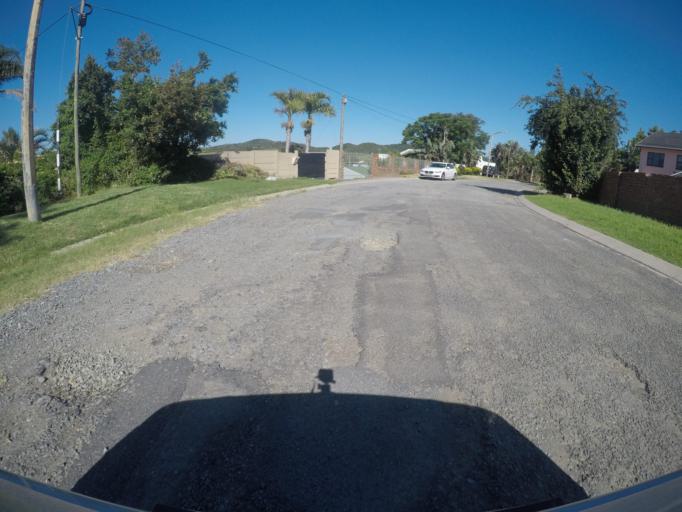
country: ZA
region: Eastern Cape
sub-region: Buffalo City Metropolitan Municipality
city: East London
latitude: -32.9506
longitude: 27.8981
